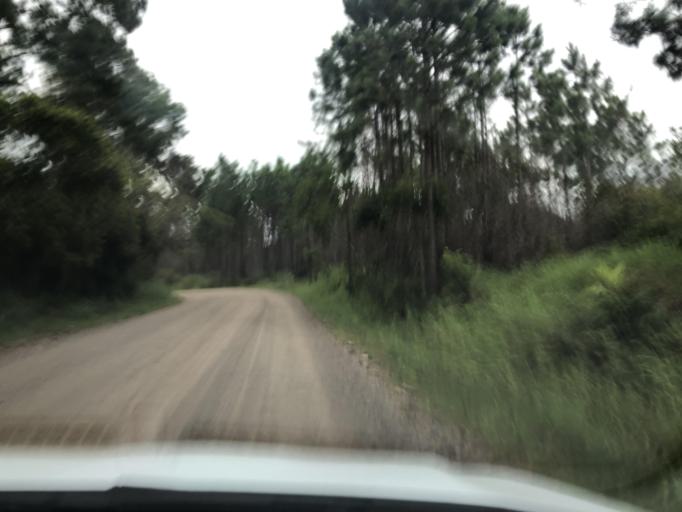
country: BR
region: Santa Catarina
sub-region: Florianopolis
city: Itacorubi
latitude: -27.5439
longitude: -48.4446
